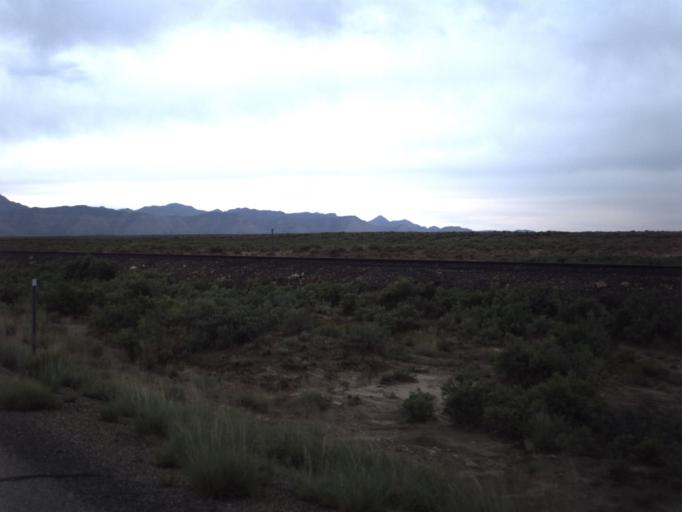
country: US
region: Utah
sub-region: Carbon County
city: East Carbon City
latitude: 39.5315
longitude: -110.5501
